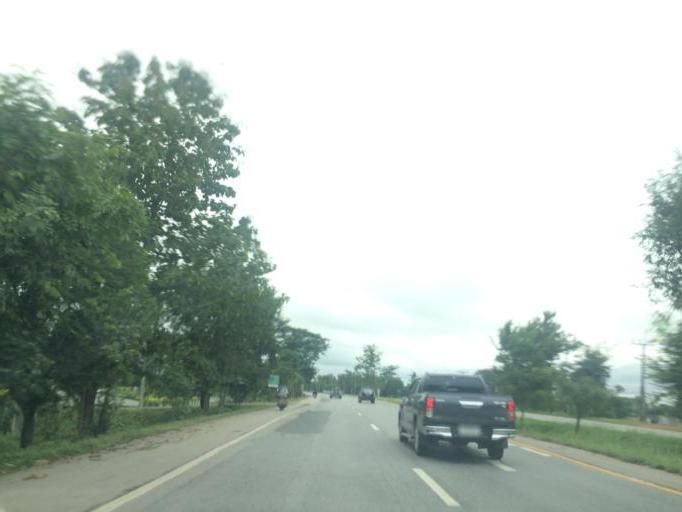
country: TH
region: Chiang Rai
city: Mae Lao
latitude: 19.7850
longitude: 99.7447
